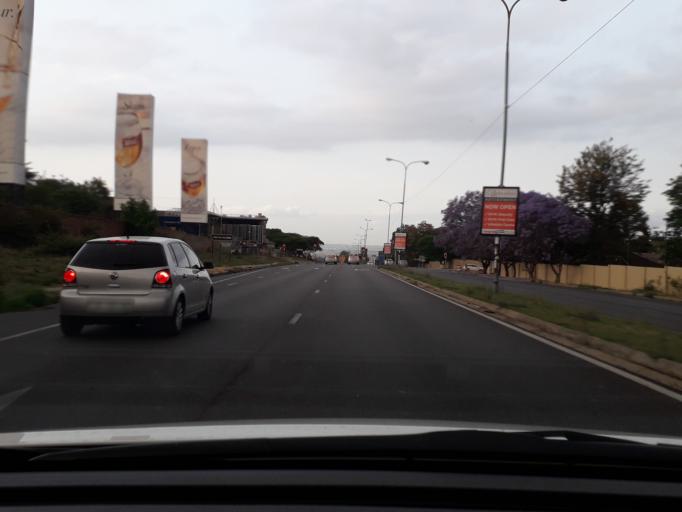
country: ZA
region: Gauteng
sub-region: City of Johannesburg Metropolitan Municipality
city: Diepsloot
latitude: -26.0485
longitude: 28.0245
